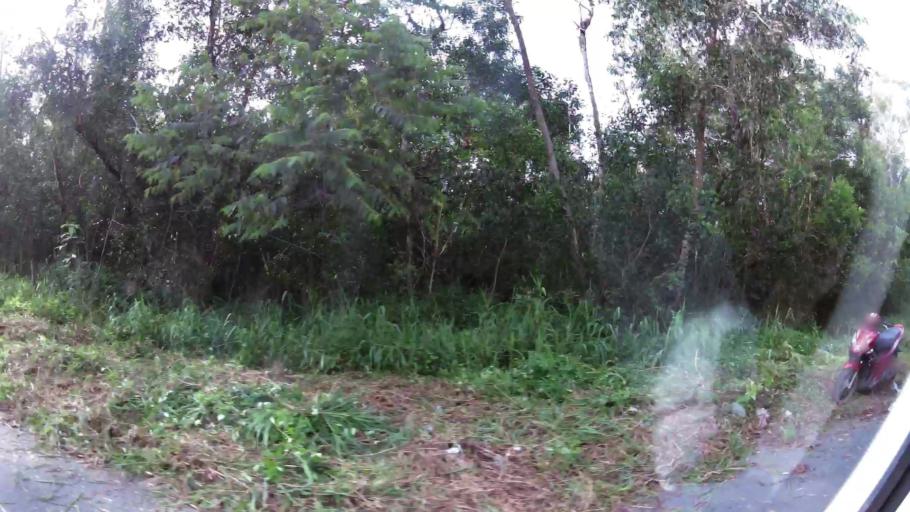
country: BN
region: Brunei and Muara
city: Bandar Seri Begawan
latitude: 4.9724
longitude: 115.0319
